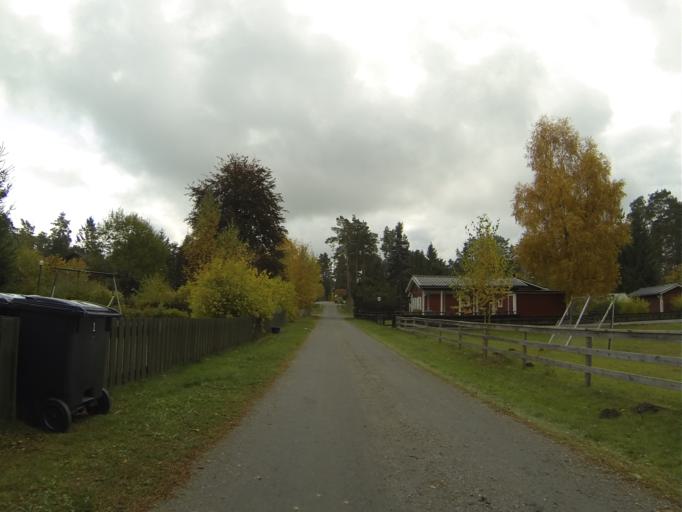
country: SE
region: Skane
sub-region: Sjobo Kommun
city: Sjoebo
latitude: 55.6346
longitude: 13.6492
